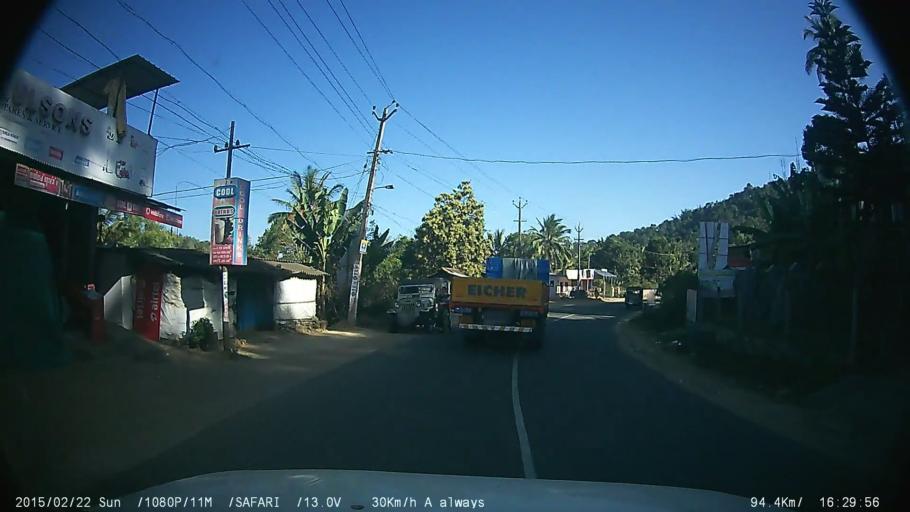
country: IN
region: Tamil Nadu
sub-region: Theni
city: Gudalur
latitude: 9.6138
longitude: 77.1564
